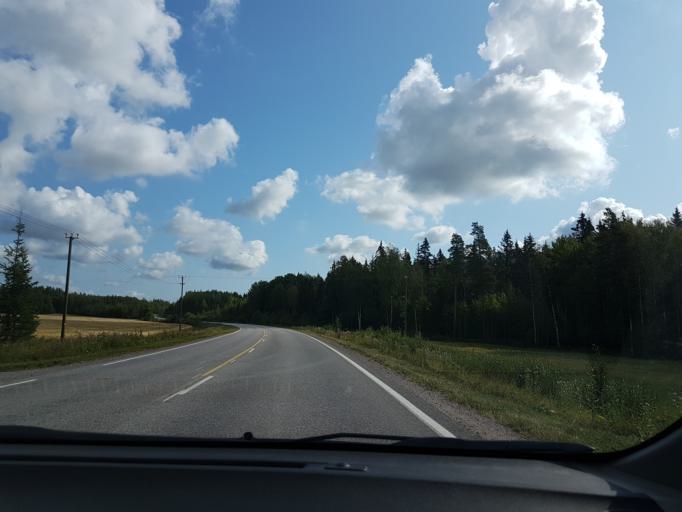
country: FI
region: Uusimaa
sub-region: Helsinki
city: Pornainen
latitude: 60.4676
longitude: 25.2908
